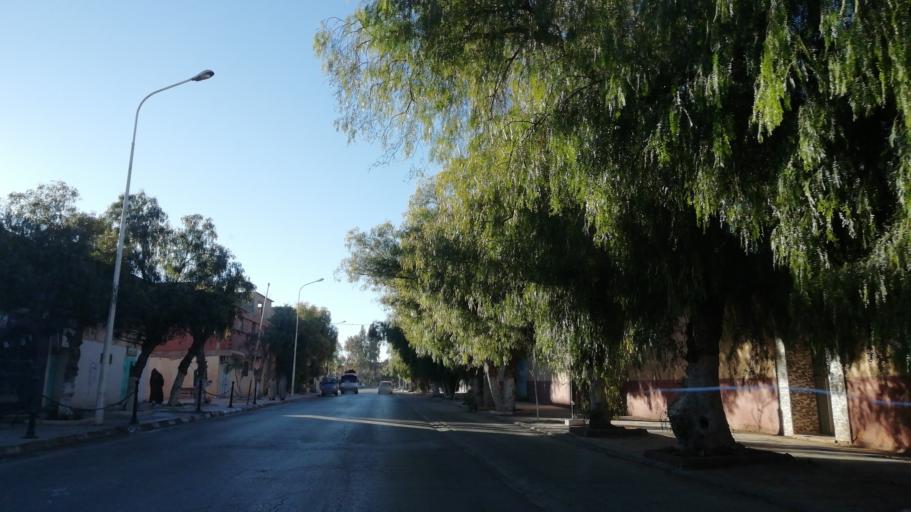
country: DZ
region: Saida
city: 'Ain el Hadjar
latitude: 34.0418
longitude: 0.0865
